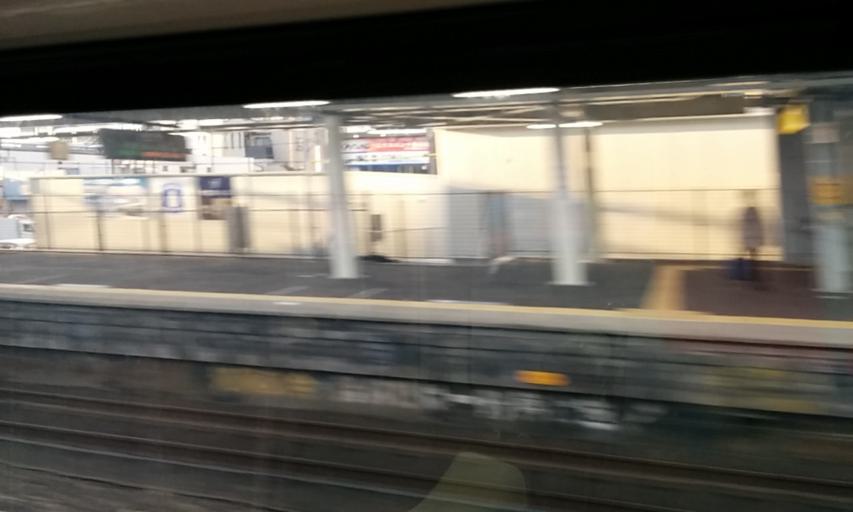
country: JP
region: Aichi
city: Kasugai
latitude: 35.2429
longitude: 136.9847
